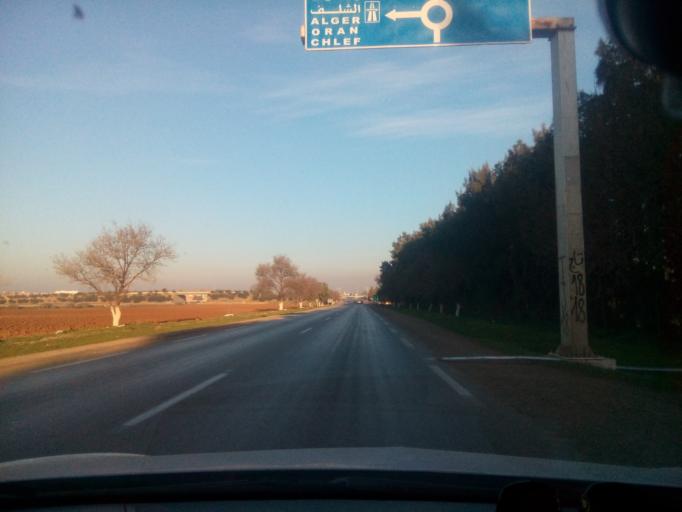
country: DZ
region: Chlef
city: Boukadir
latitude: 36.0550
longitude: 1.1031
